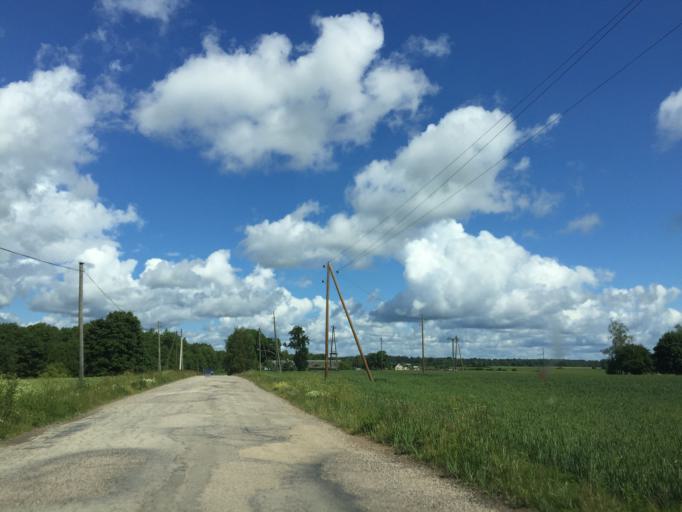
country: LV
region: Lecava
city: Iecava
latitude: 56.6089
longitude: 24.1912
